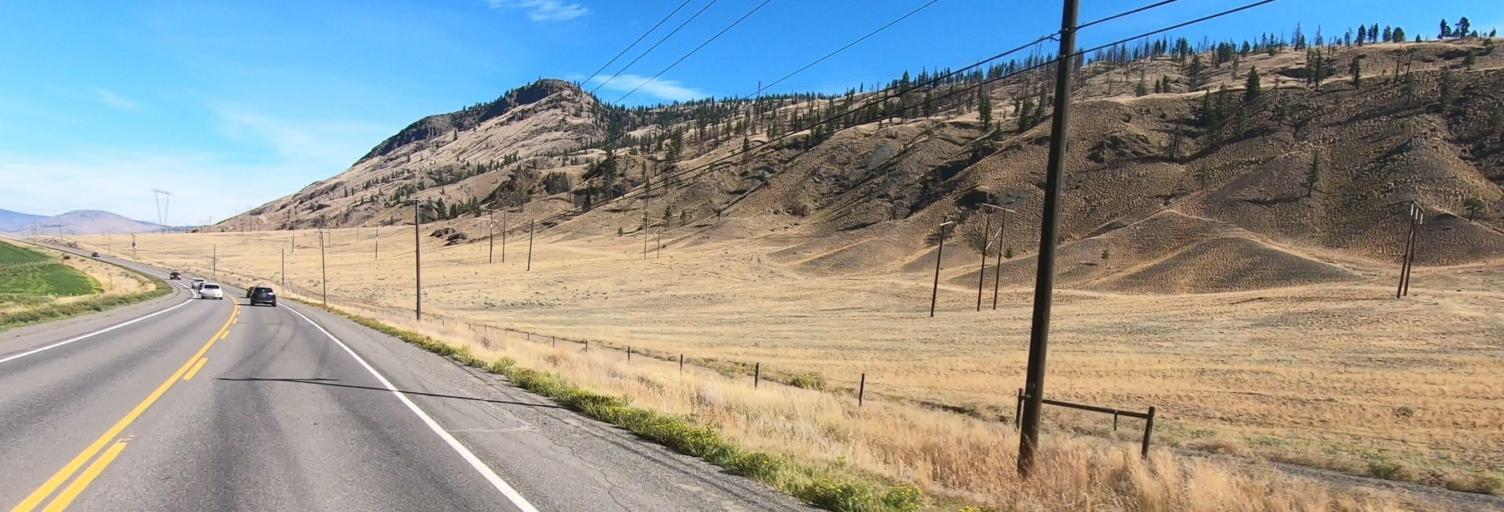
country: CA
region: British Columbia
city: Cache Creek
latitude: 50.8566
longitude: -121.3844
